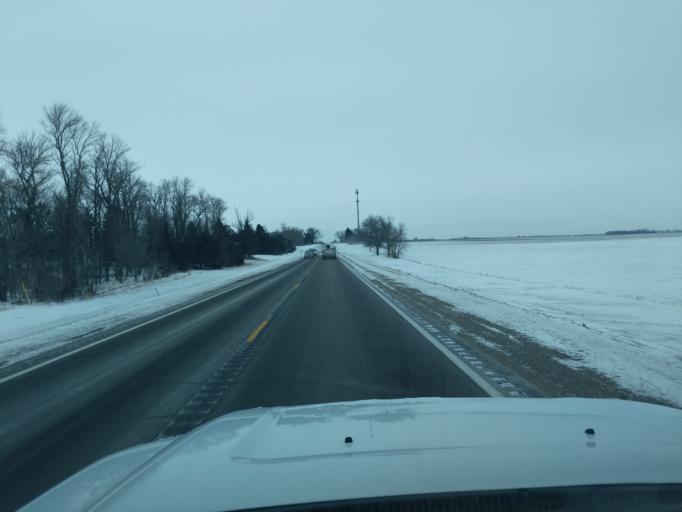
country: US
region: Minnesota
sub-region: Redwood County
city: Redwood Falls
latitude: 44.6033
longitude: -94.9945
